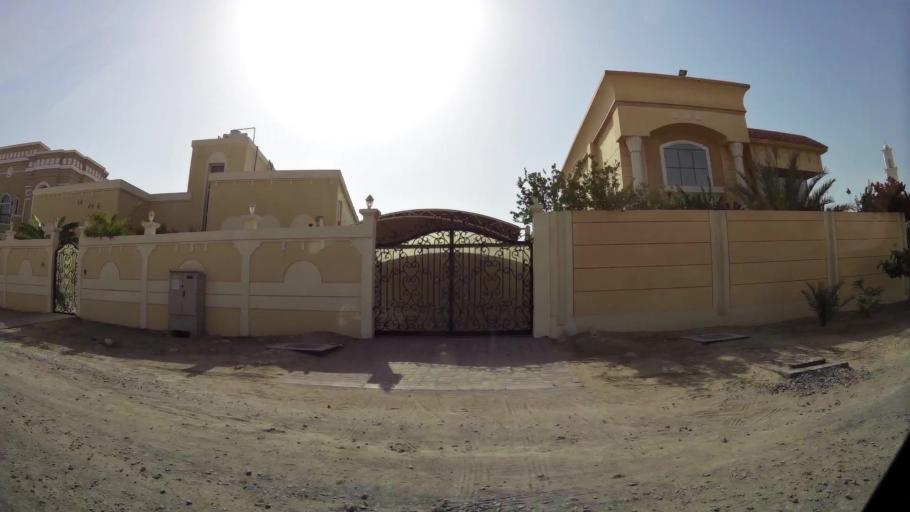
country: AE
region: Dubai
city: Dubai
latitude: 25.1603
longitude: 55.2659
